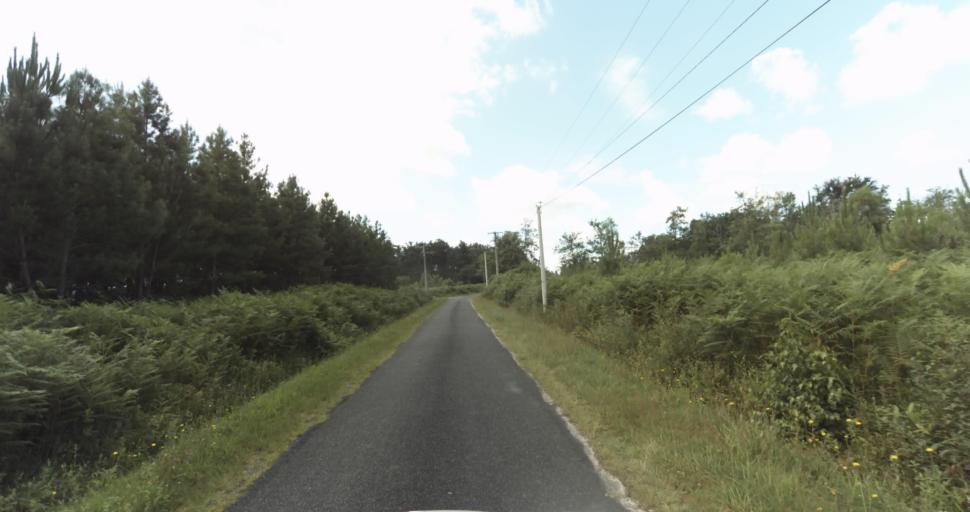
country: FR
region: Aquitaine
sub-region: Departement de la Gironde
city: Bazas
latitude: 44.4530
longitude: -0.2170
